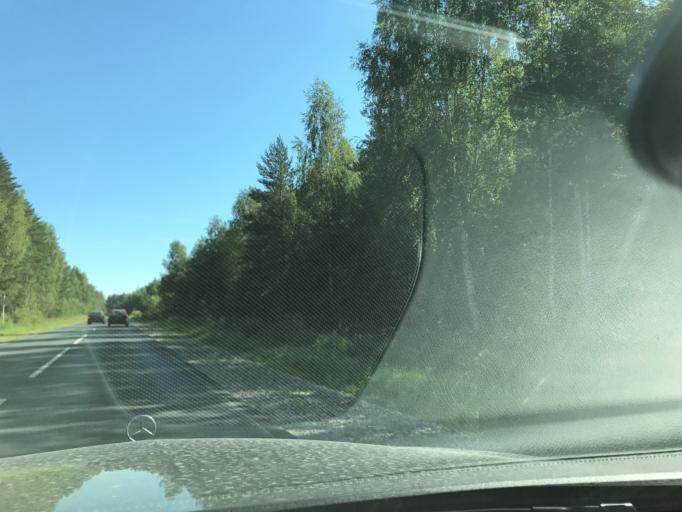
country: RU
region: Vladimir
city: Kirzhach
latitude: 56.1815
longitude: 38.9100
